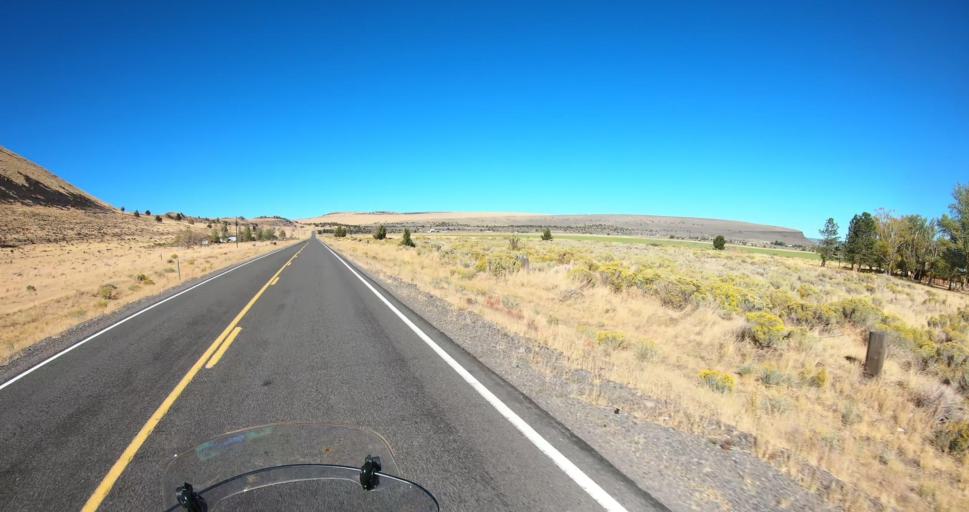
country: US
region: Oregon
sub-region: Lake County
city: Lakeview
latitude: 42.9912
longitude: -120.7767
